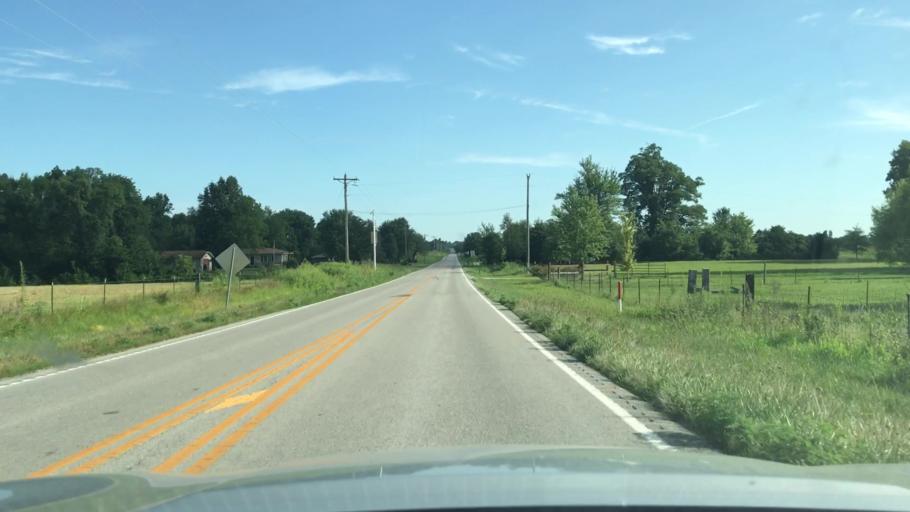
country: US
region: Kentucky
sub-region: Todd County
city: Elkton
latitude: 36.9148
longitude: -87.1631
